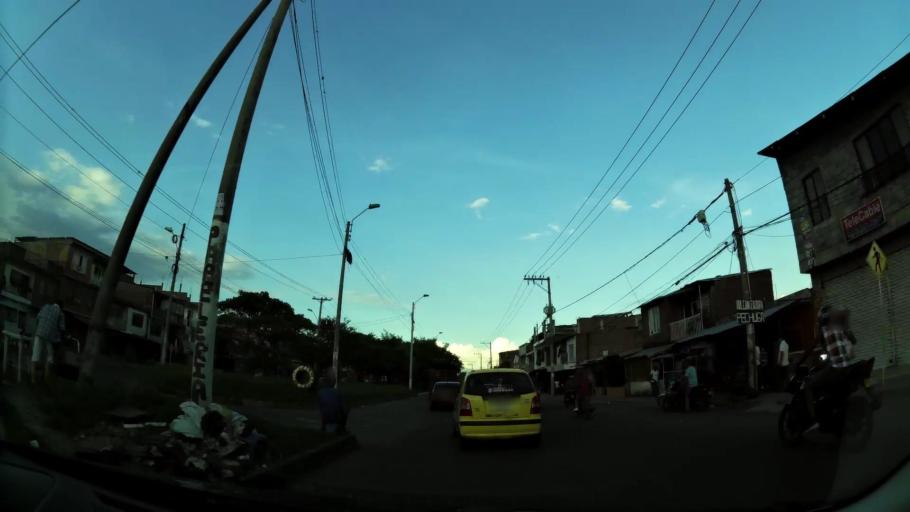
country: CO
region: Valle del Cauca
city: Cali
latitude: 3.4114
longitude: -76.4923
